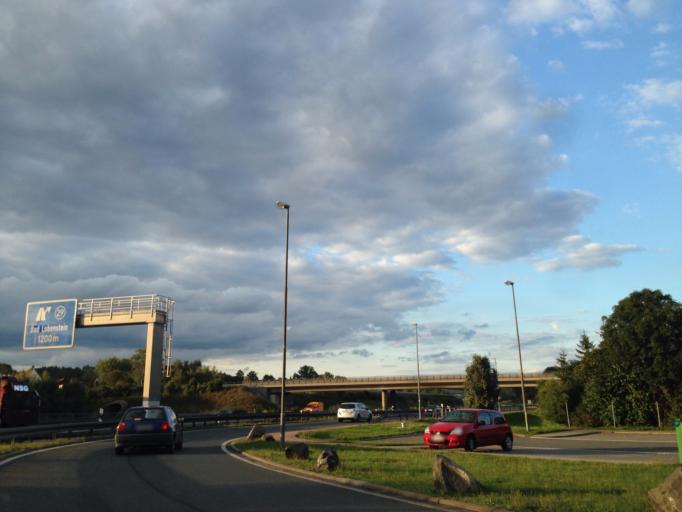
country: DE
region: Thuringia
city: Birkenhugel
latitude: 50.4278
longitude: 11.7954
